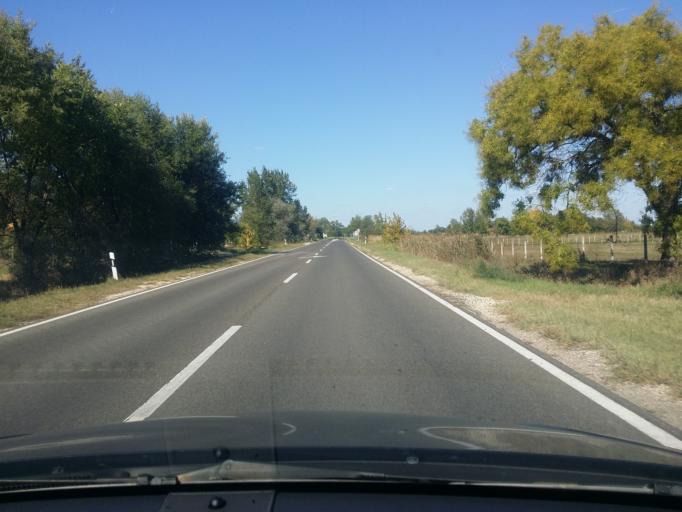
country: HU
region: Bacs-Kiskun
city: Palmonostora
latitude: 46.6336
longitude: 19.8933
